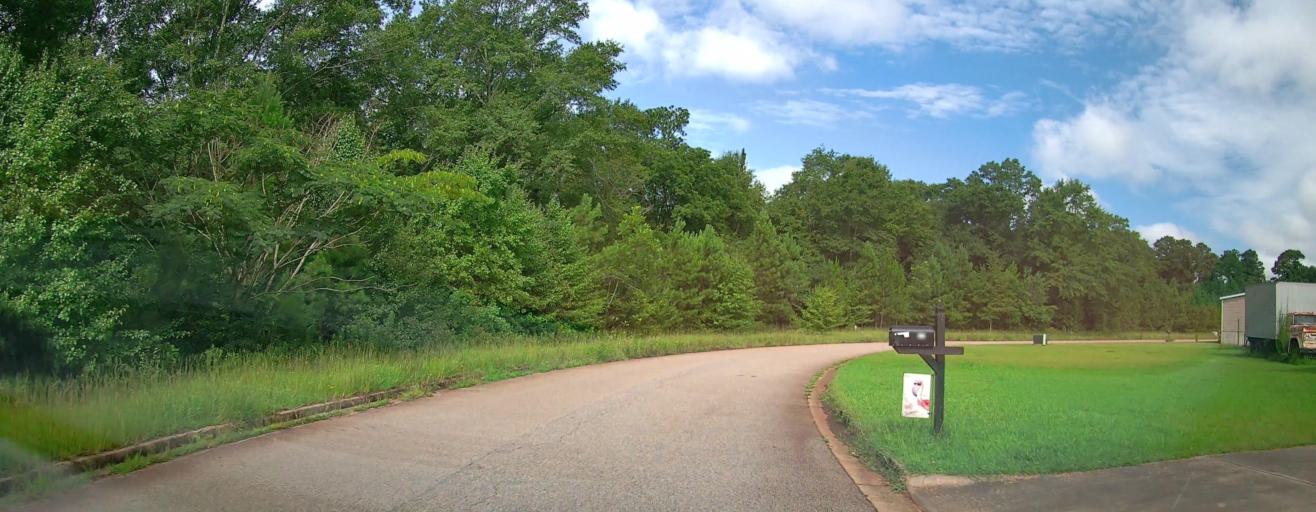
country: US
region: Georgia
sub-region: Houston County
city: Centerville
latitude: 32.6448
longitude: -83.7214
